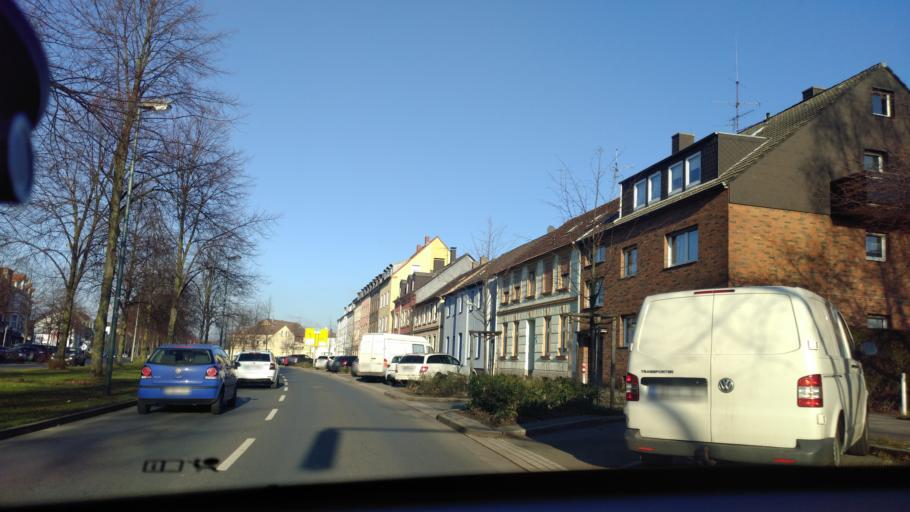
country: DE
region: North Rhine-Westphalia
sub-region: Regierungsbezirk Dusseldorf
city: Essen
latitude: 51.4985
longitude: 7.0106
